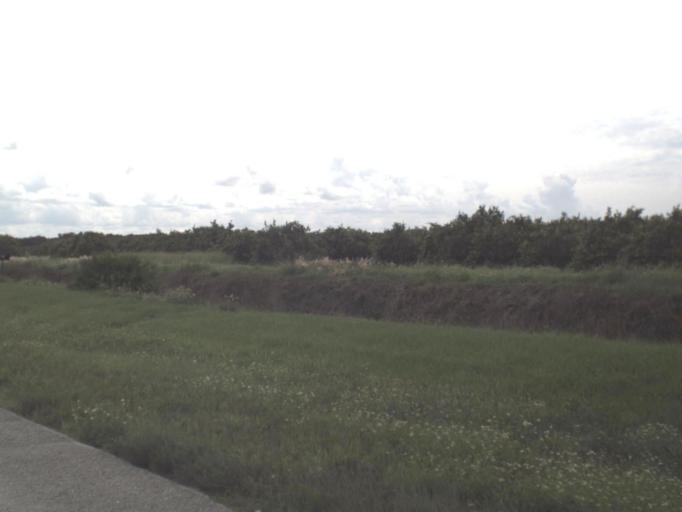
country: US
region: Florida
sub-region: DeSoto County
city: Southeast Arcadia
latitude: 27.2014
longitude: -81.8296
